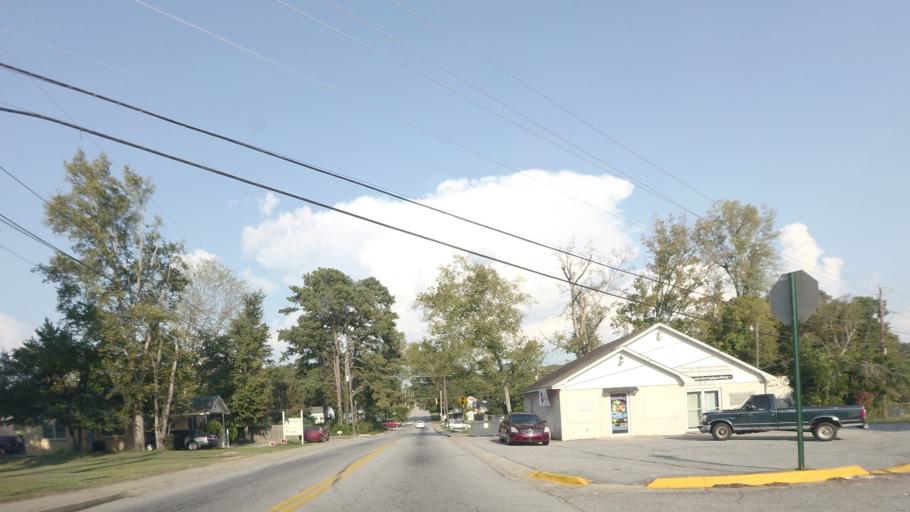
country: US
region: Georgia
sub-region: Bibb County
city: Macon
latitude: 32.8470
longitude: -83.6893
